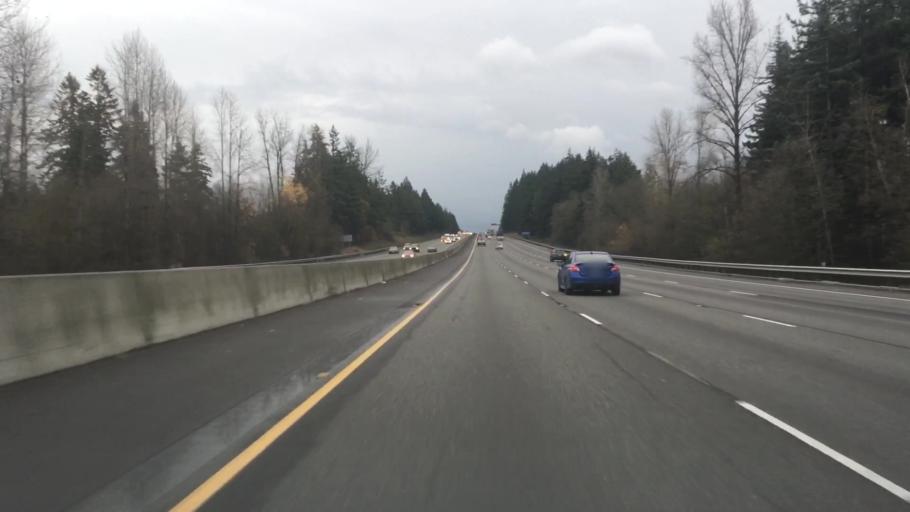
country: US
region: Washington
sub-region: Thurston County
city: Grand Mound
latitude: 46.8881
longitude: -122.9636
